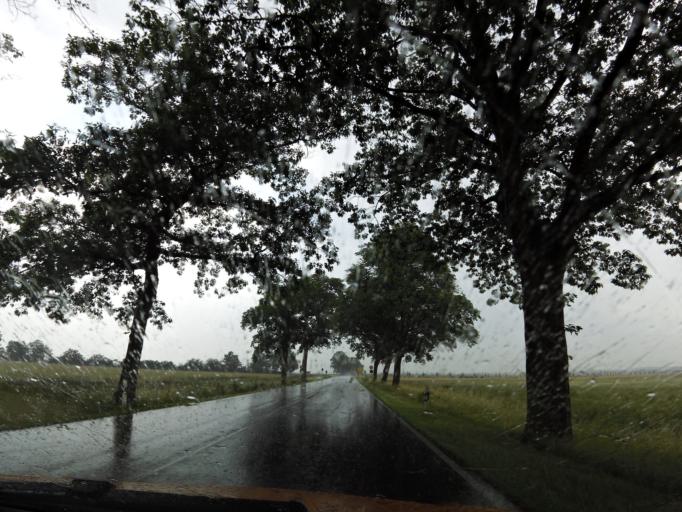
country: DE
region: Brandenburg
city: Pessin
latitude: 52.6634
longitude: 12.6308
